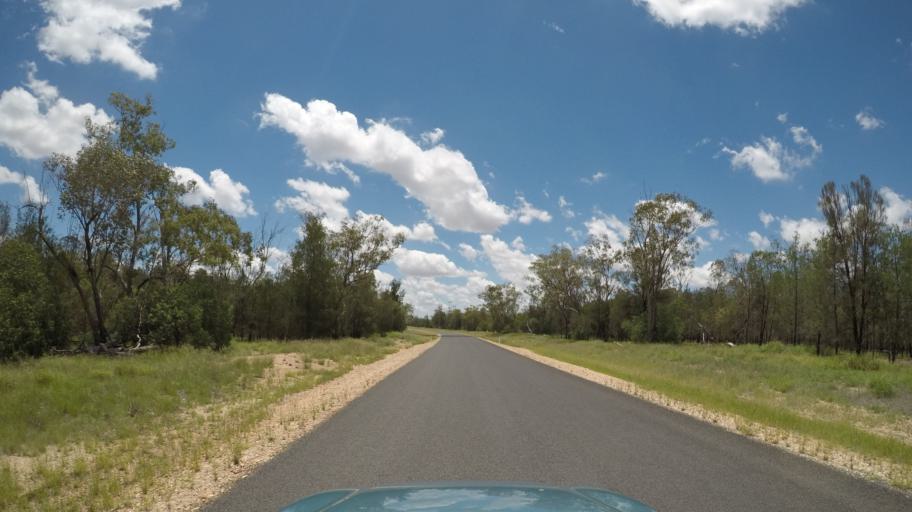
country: AU
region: Queensland
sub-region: Goondiwindi
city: Goondiwindi
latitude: -28.1555
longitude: 150.1219
